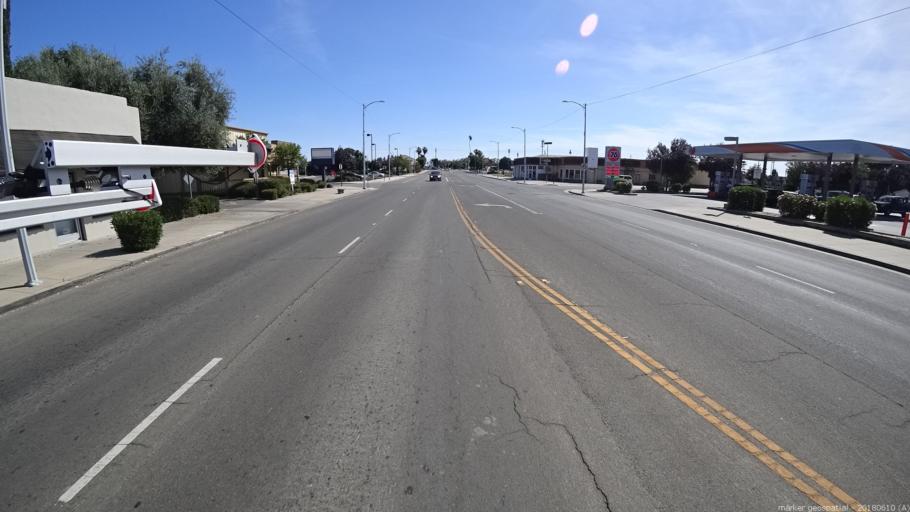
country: US
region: California
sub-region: Madera County
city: Chowchilla
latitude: 37.1232
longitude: -120.2596
